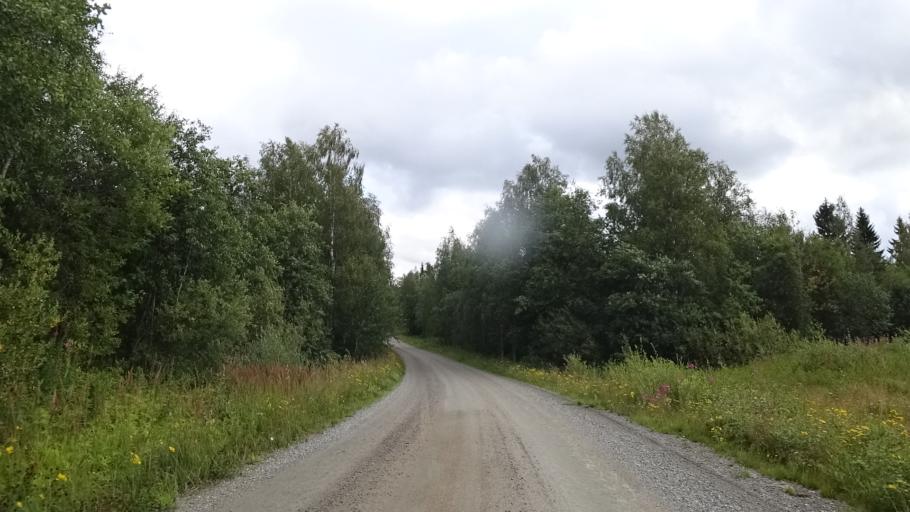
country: FI
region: North Karelia
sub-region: Joensuu
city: Ilomantsi
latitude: 62.9335
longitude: 31.3004
